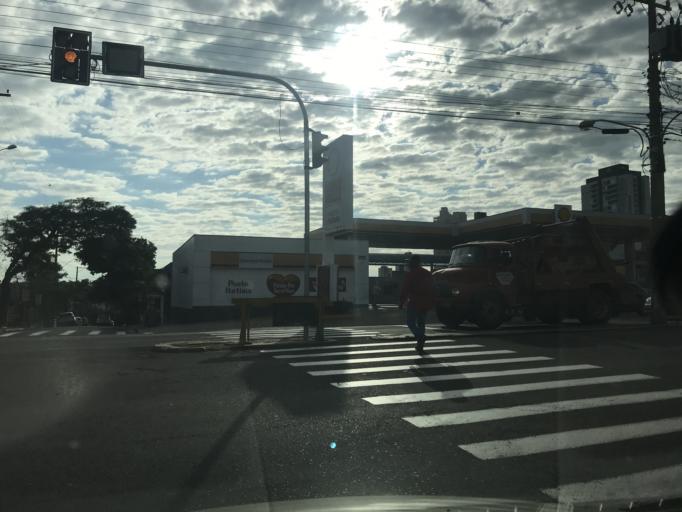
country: BR
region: Sao Paulo
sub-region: Presidente Prudente
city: Presidente Prudente
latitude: -22.1222
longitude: -51.3960
